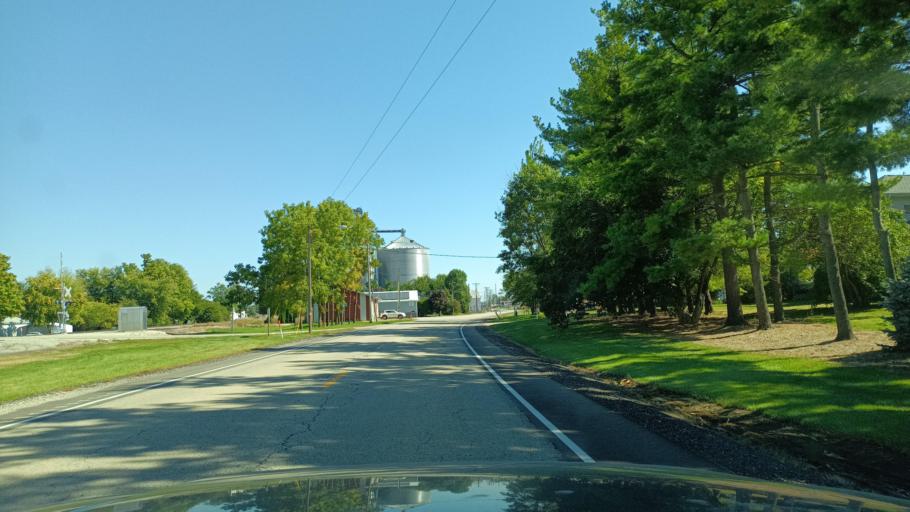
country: US
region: Illinois
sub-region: Woodford County
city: Eureka
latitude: 40.6281
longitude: -89.2829
